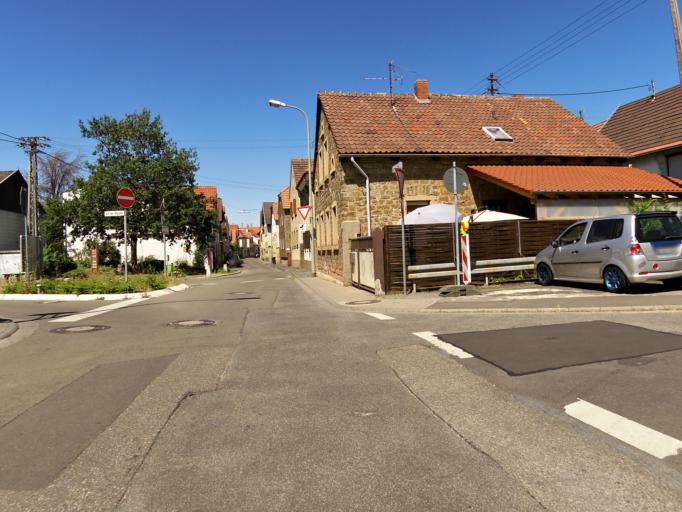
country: DE
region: Rheinland-Pfalz
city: Neustadt
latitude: 49.3669
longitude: 8.1731
